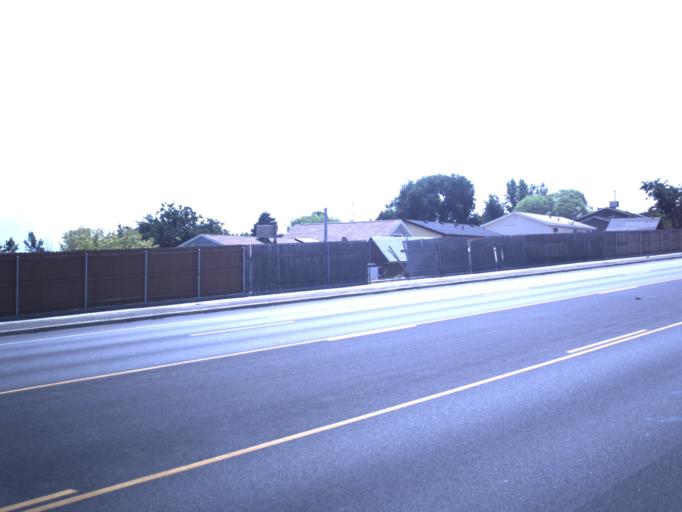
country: US
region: Utah
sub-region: Salt Lake County
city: Kearns
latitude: 40.6646
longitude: -112.0248
